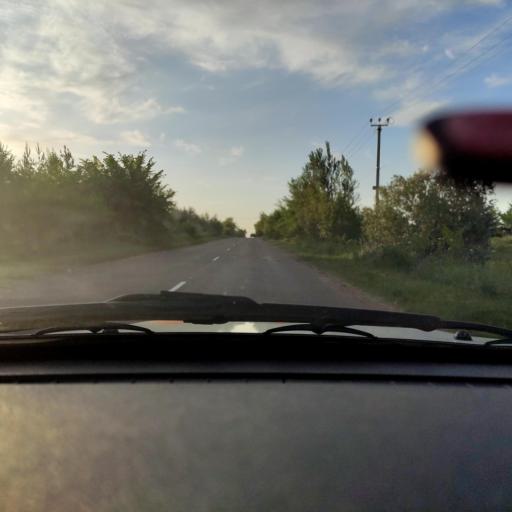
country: RU
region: Voronezj
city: Podgornoye
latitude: 51.8321
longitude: 39.2049
